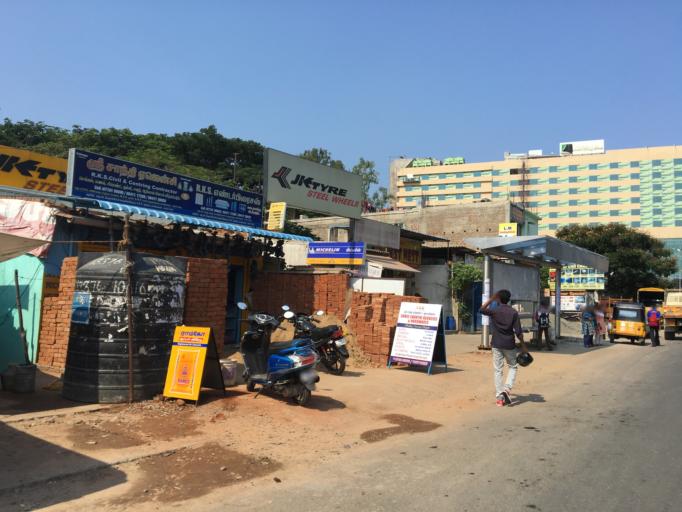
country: IN
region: Tamil Nadu
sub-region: Kancheepuram
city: Perungudi
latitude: 12.9803
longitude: 80.2513
